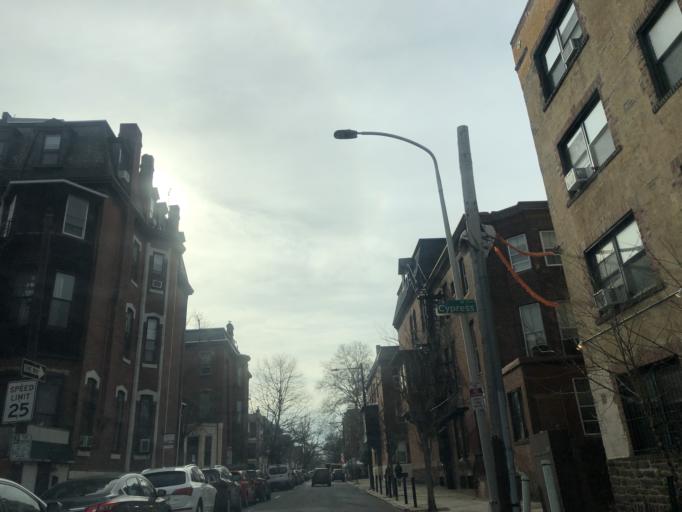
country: US
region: Pennsylvania
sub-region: Philadelphia County
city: Philadelphia
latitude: 39.9486
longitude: -75.1790
